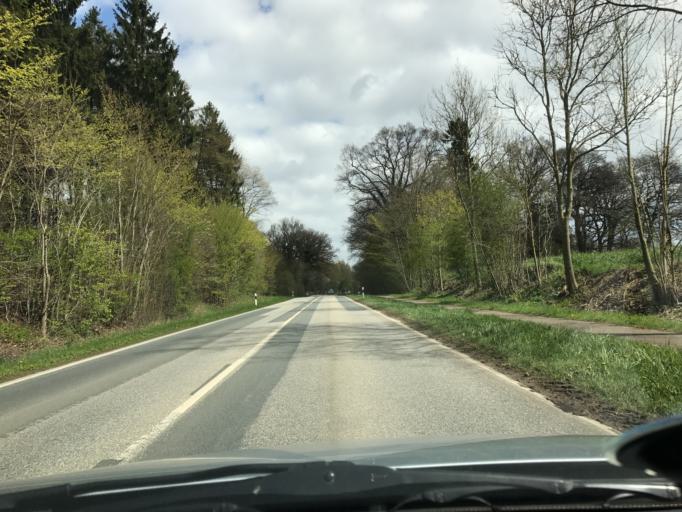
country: DE
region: Schleswig-Holstein
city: Susel
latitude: 54.0893
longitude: 10.7356
